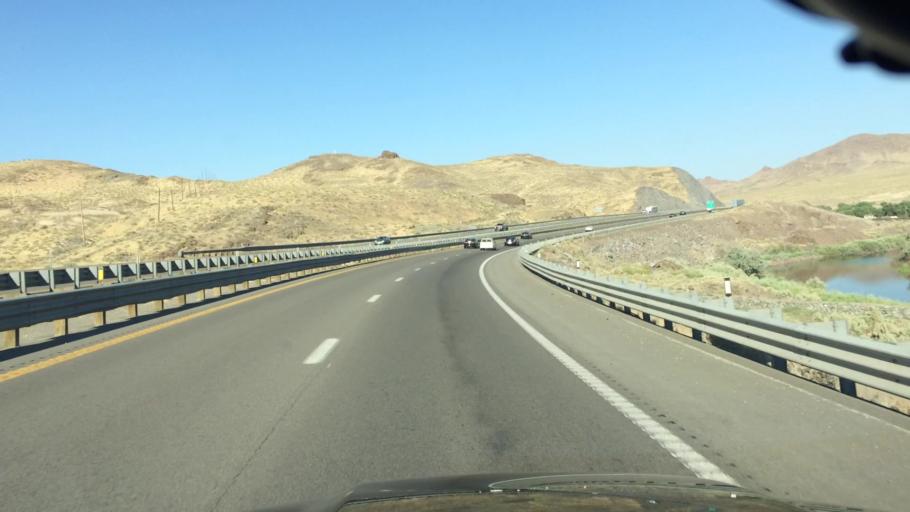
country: US
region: Nevada
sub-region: Lyon County
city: Fernley
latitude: 39.5910
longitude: -119.3839
